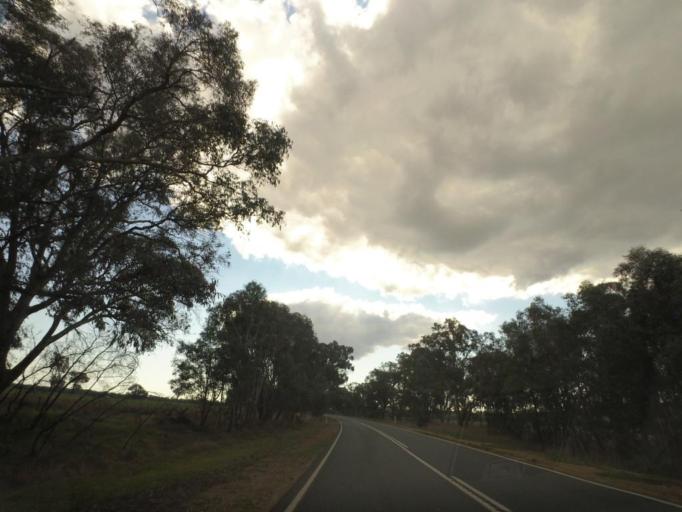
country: AU
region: New South Wales
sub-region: Corowa Shire
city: Howlong
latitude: -36.1980
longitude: 146.6197
